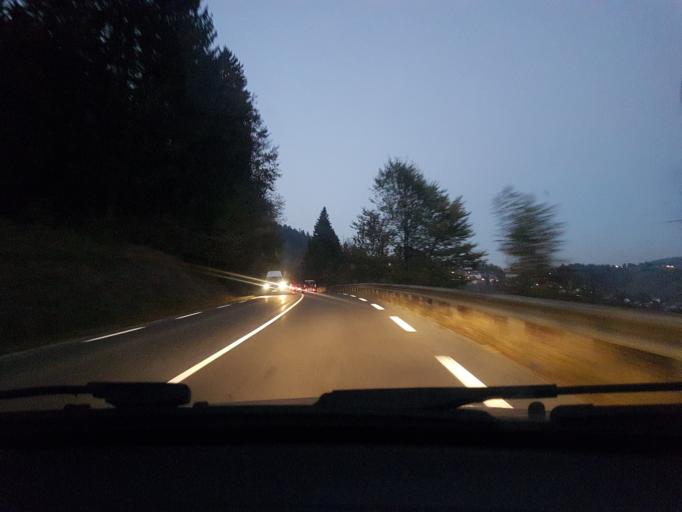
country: FR
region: Franche-Comte
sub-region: Departement du Doubs
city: Les Fins
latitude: 47.0723
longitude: 6.6168
